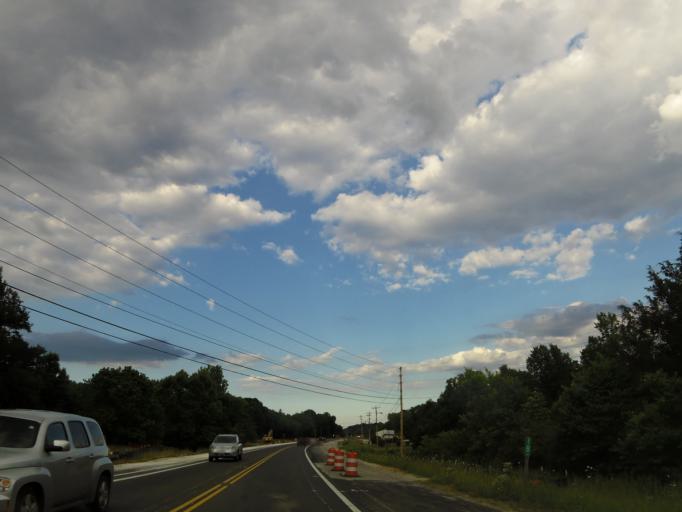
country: US
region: Tennessee
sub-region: Maury County
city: Columbia
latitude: 35.6366
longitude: -86.9962
